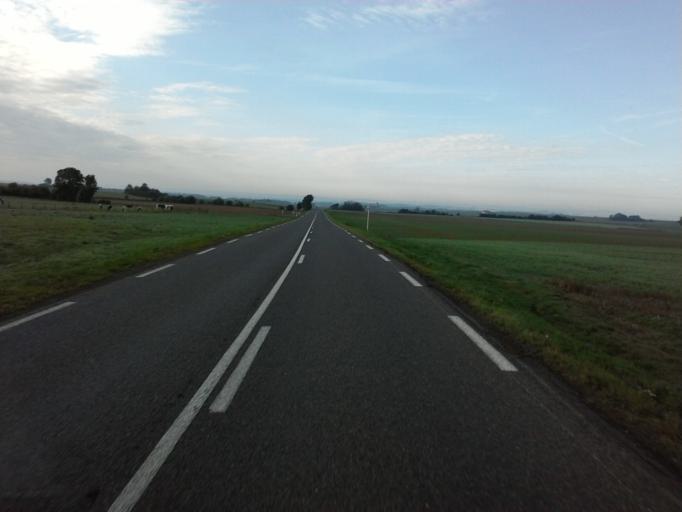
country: FR
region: Lorraine
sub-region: Departement de Meurthe-et-Moselle
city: Longuyon
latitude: 49.4919
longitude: 5.6142
